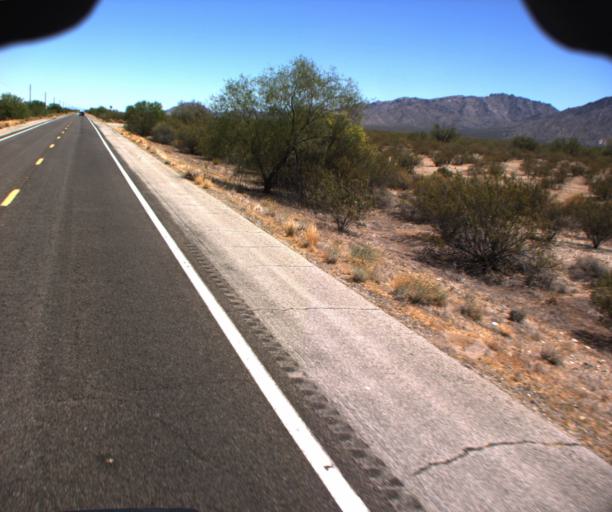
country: US
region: Arizona
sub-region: La Paz County
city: Salome
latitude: 33.8616
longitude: -113.4180
